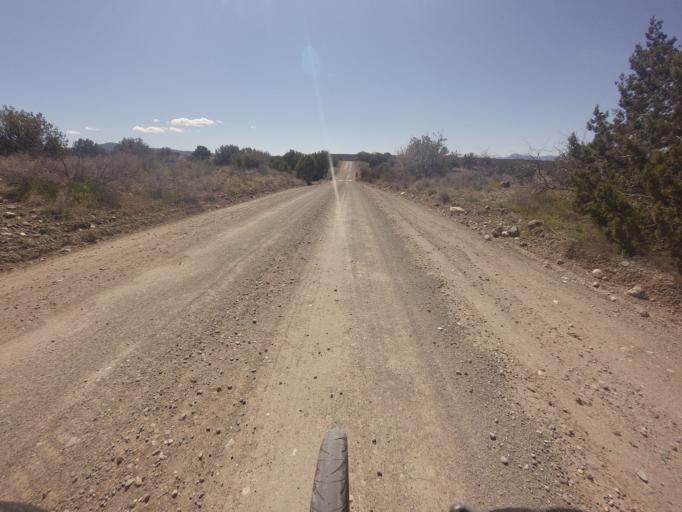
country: US
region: Arizona
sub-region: Yavapai County
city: Lake Montezuma
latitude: 34.6214
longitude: -111.7238
